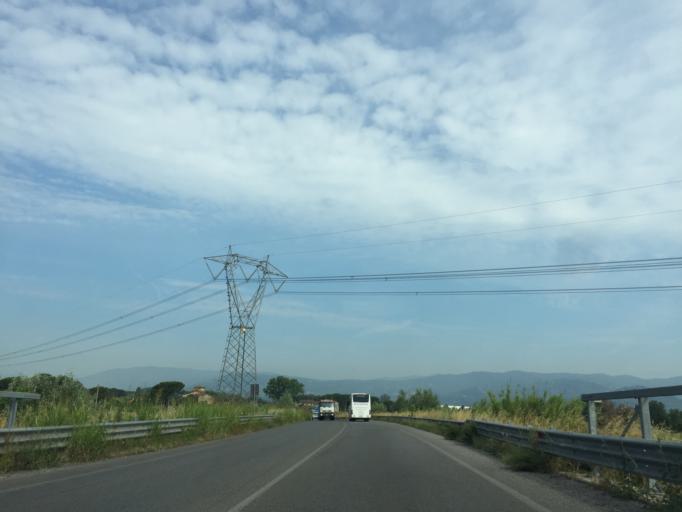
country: IT
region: Tuscany
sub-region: Provincia di Pistoia
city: Cintolese
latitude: 43.8478
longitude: 10.8113
